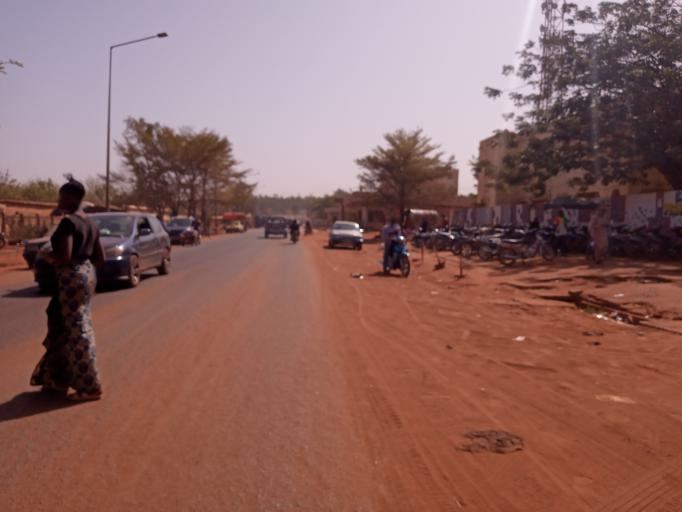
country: ML
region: Bamako
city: Bamako
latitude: 12.6076
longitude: -8.0015
